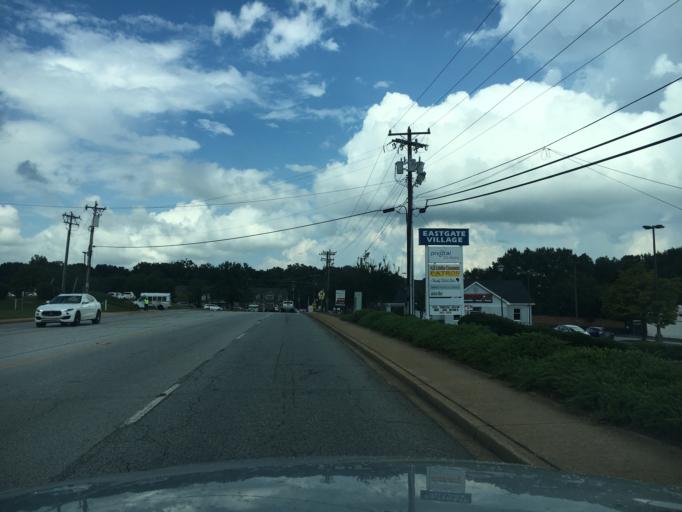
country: US
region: South Carolina
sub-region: Greenville County
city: Taylors
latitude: 34.8907
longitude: -82.2964
